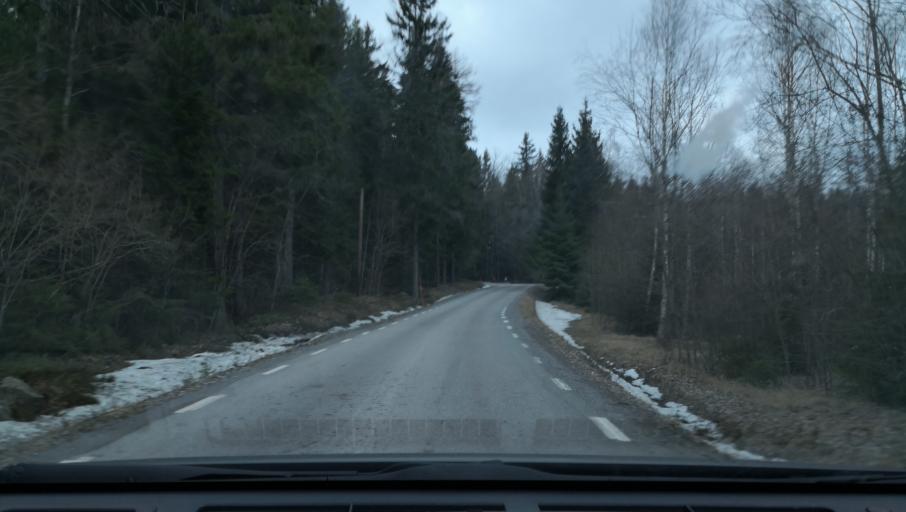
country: SE
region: Vaestmanland
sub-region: Kopings Kommun
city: Kolsva
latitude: 59.5696
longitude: 15.7258
